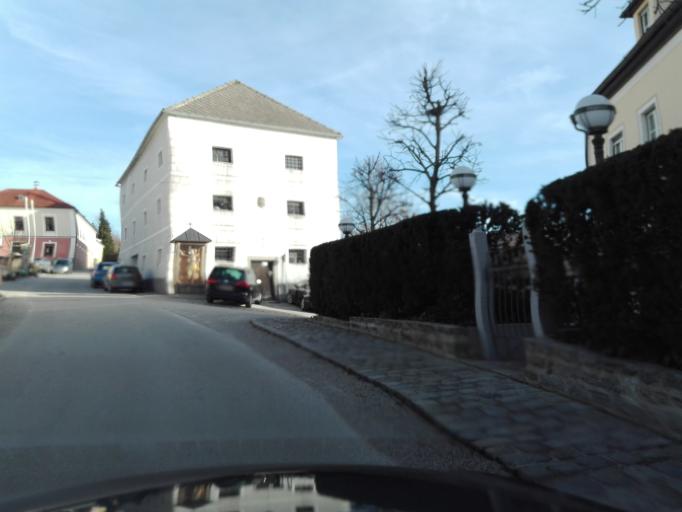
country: AT
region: Lower Austria
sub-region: Politischer Bezirk Amstetten
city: Amstetten
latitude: 48.1609
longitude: 14.8448
